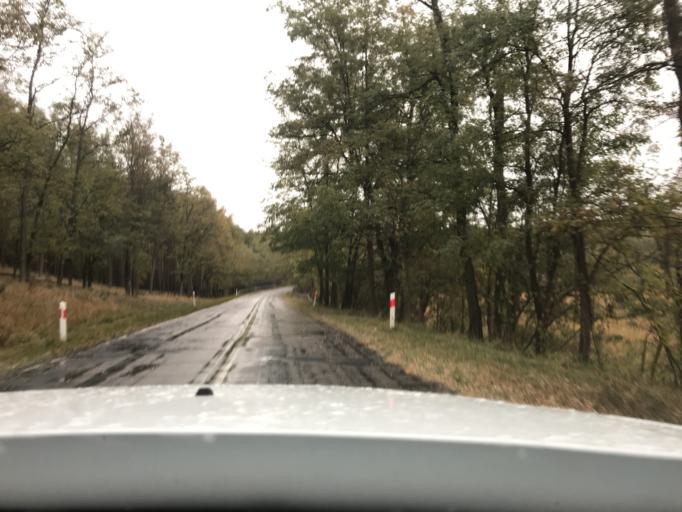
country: DE
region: Brandenburg
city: Neulewin
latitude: 52.7727
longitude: 14.3040
